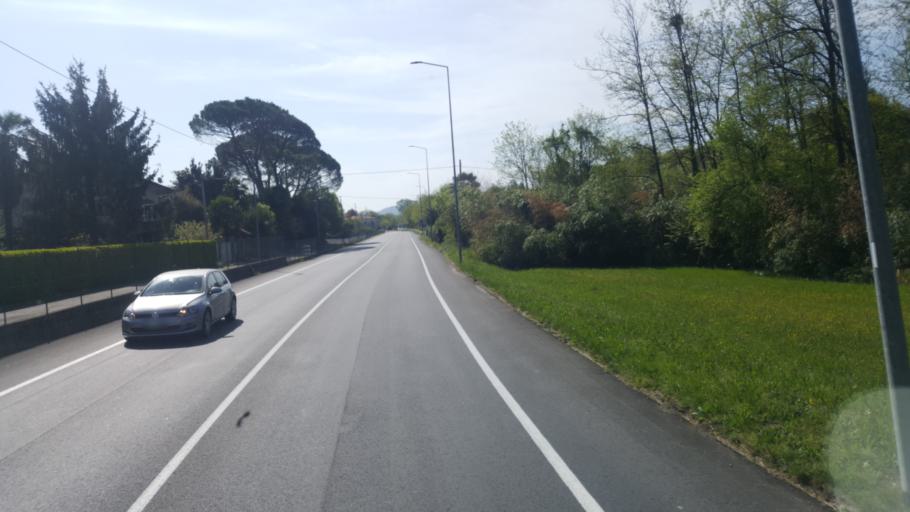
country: IT
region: Lombardy
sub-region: Provincia di Varese
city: Barasso
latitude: 45.8172
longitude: 8.7598
